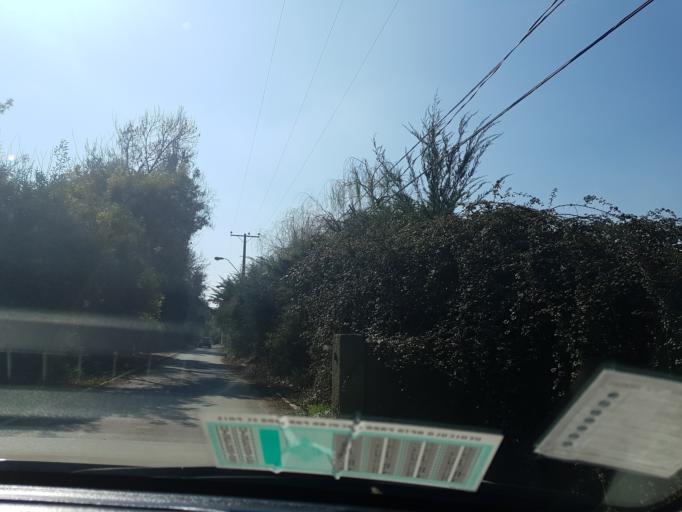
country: CL
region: Santiago Metropolitan
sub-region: Provincia de Cordillera
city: Puente Alto
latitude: -33.6279
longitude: -70.5601
